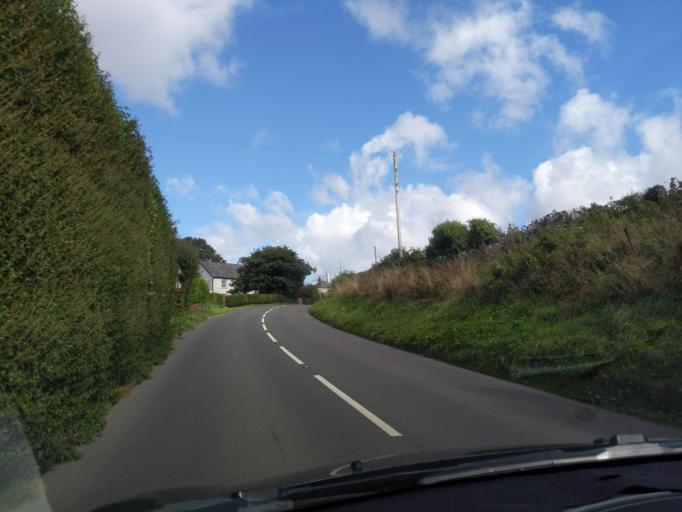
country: GB
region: England
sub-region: Devon
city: Holsworthy
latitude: 50.8818
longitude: -4.2927
